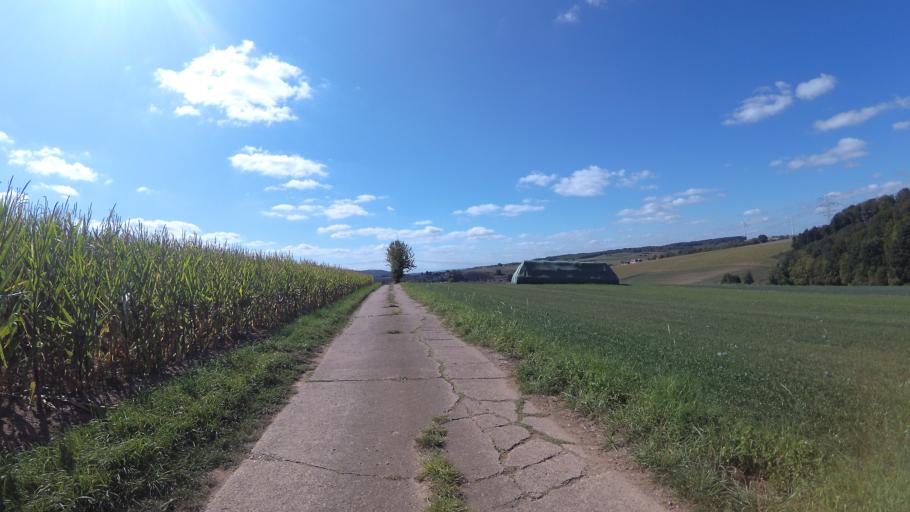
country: DE
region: Saarland
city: Lebach
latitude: 49.4314
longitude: 6.9310
